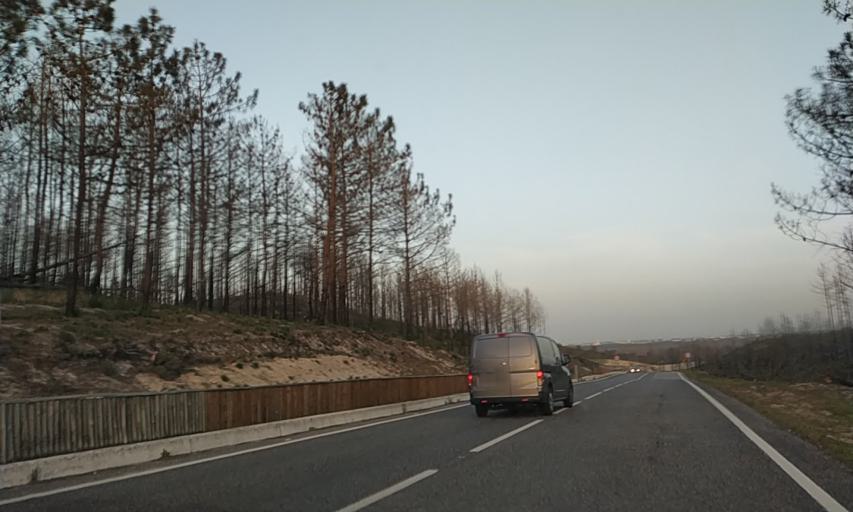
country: PT
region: Leiria
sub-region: Marinha Grande
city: Marinha Grande
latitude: 39.7461
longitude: -8.9911
